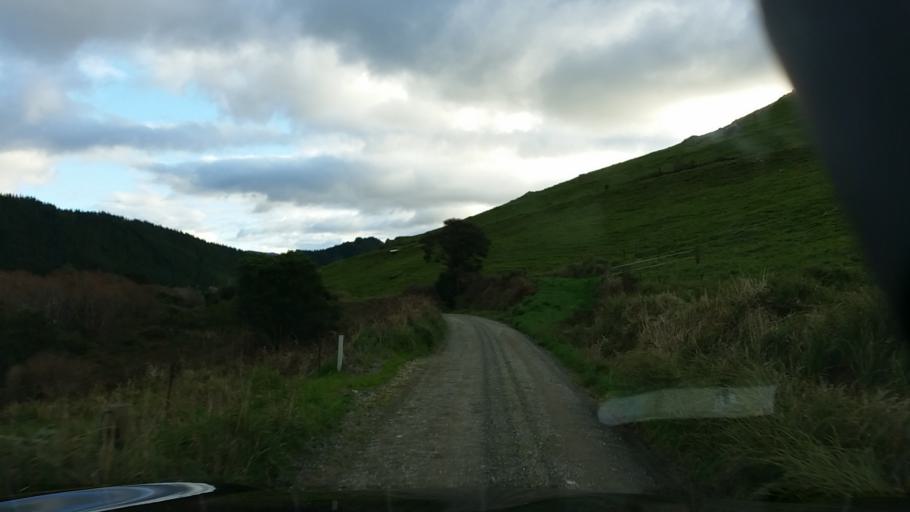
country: NZ
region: Nelson
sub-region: Nelson City
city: Nelson
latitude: -41.2087
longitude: 173.6342
